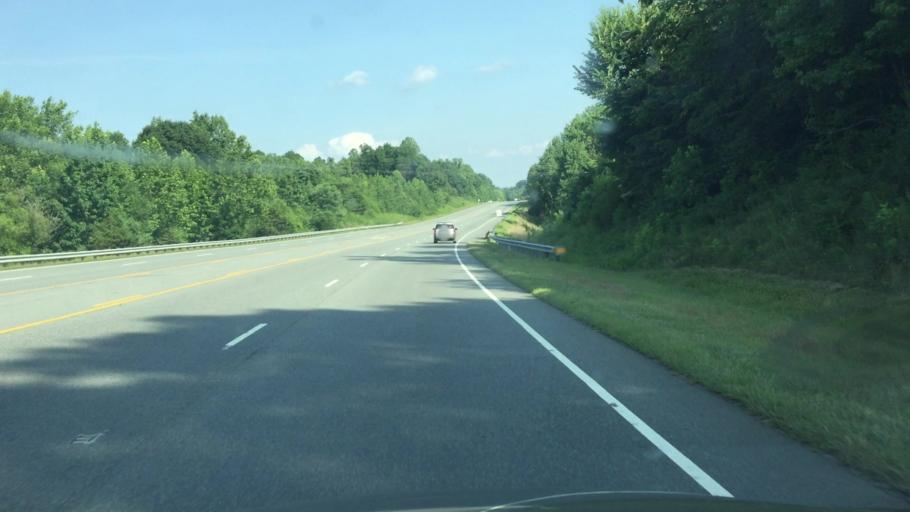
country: US
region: North Carolina
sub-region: Rockingham County
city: Reidsville
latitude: 36.3725
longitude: -79.6486
